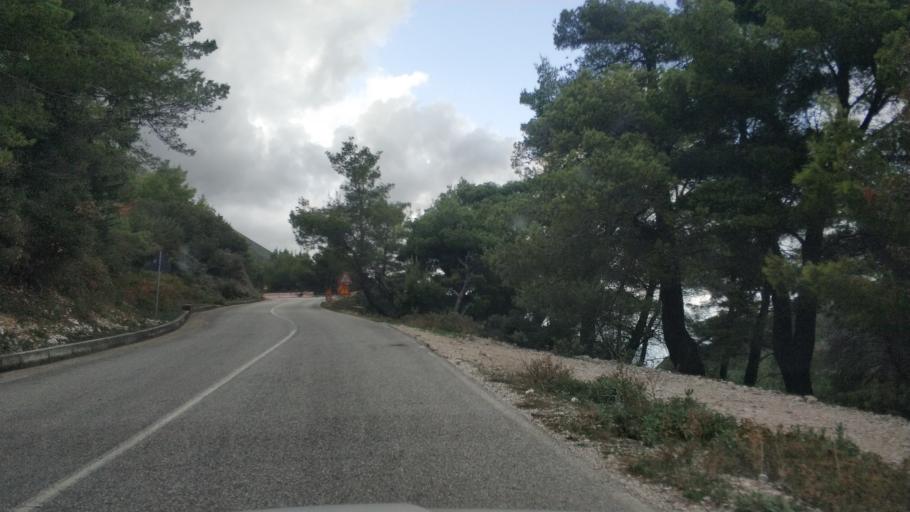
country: AL
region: Vlore
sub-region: Rrethi i Vlores
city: Orikum
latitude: 40.2509
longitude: 19.5414
